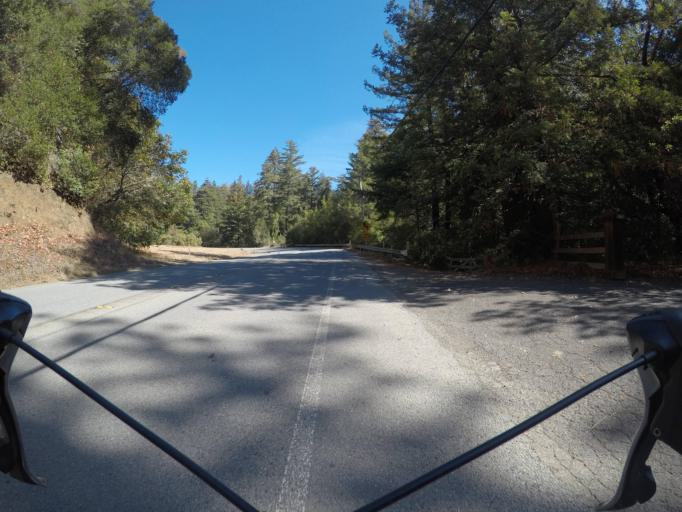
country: US
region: California
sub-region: San Mateo County
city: Portola Valley
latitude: 37.3233
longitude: -122.2734
